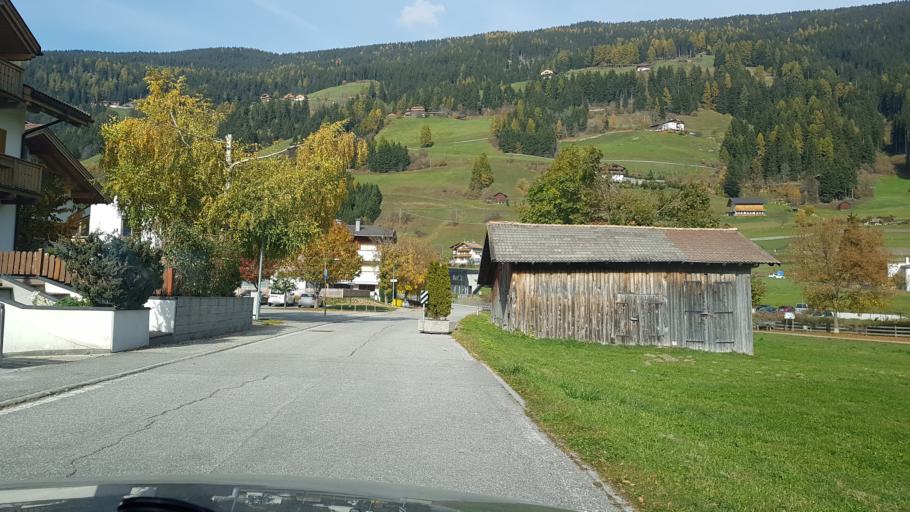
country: IT
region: Trentino-Alto Adige
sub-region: Bolzano
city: San Candido
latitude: 46.7324
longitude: 12.2885
